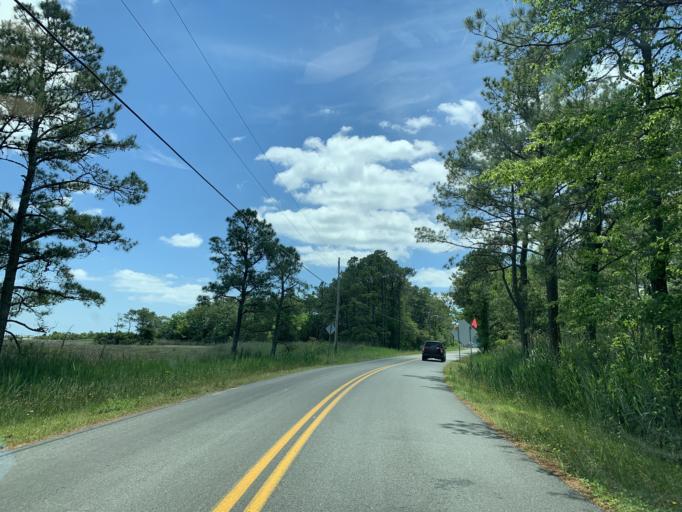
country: US
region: Maryland
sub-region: Worcester County
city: West Ocean City
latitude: 38.3143
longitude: -75.1189
